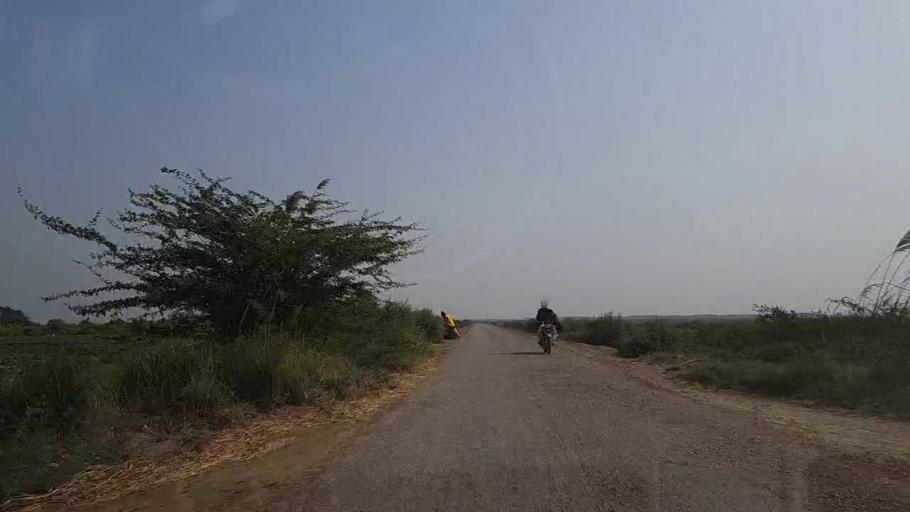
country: PK
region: Sindh
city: Keti Bandar
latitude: 24.2338
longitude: 67.6438
